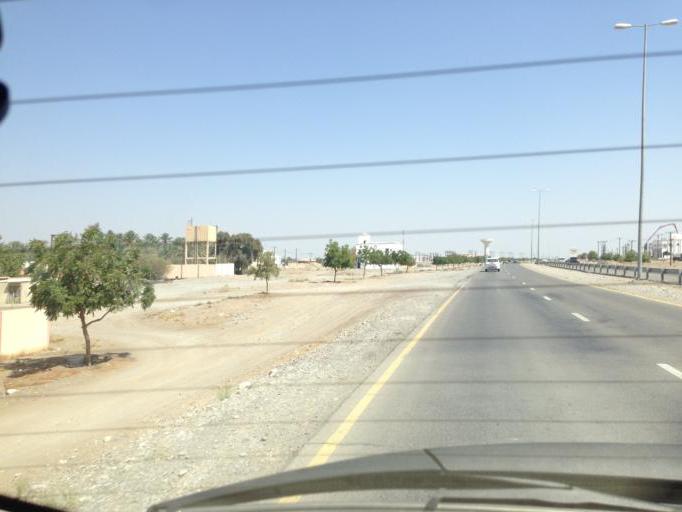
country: OM
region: Al Batinah
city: Rustaq
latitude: 23.5371
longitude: 57.4698
